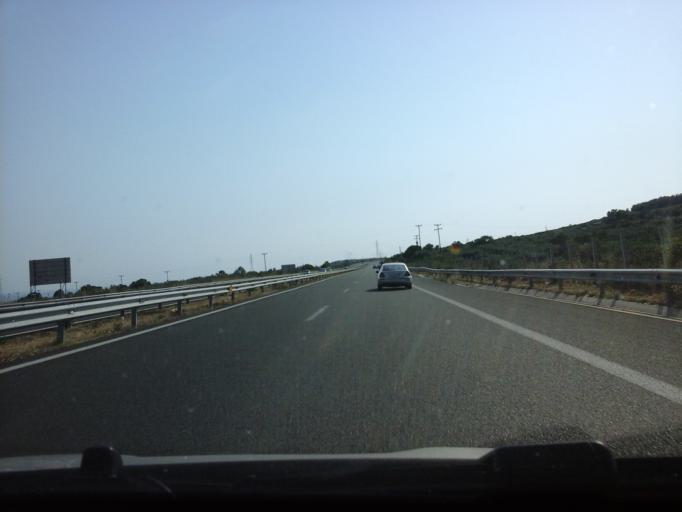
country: GR
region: East Macedonia and Thrace
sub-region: Nomos Evrou
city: Alexandroupoli
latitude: 40.8654
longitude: 25.7660
